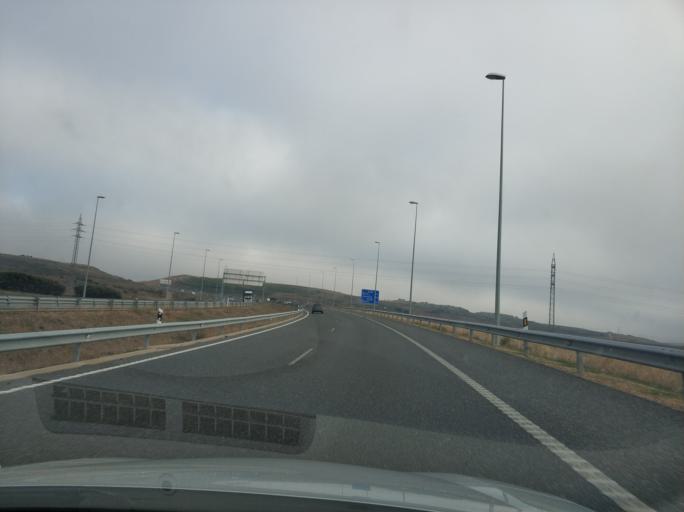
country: ES
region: Castille and Leon
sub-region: Provincia de Leon
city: Leon
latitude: 42.5655
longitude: -5.5426
